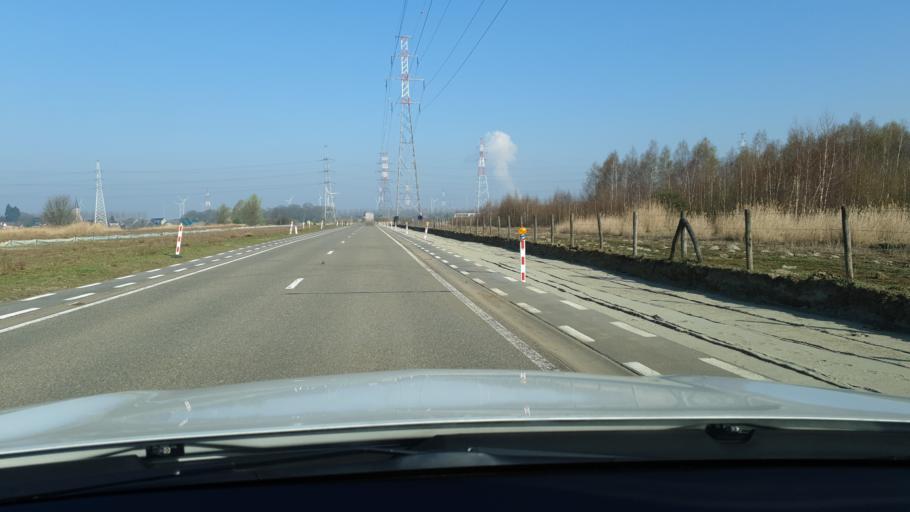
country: BE
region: Flanders
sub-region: Provincie Oost-Vlaanderen
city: Beveren
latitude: 51.2454
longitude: 4.2880
